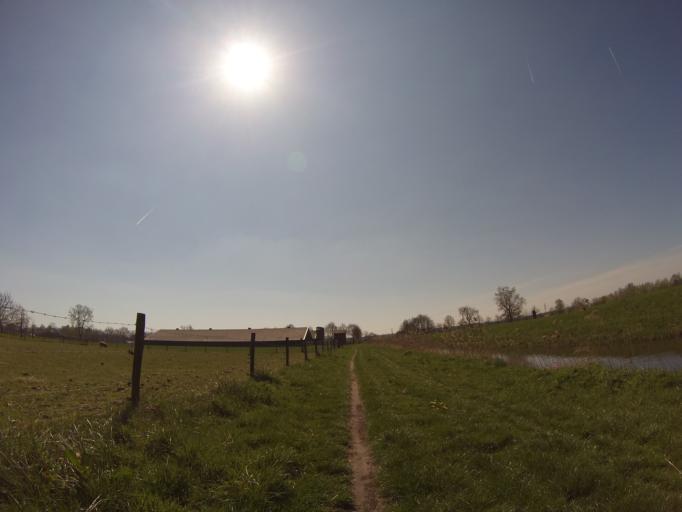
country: NL
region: Utrecht
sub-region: Gemeente Utrechtse Heuvelrug
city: Overberg
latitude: 52.0539
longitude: 5.4843
